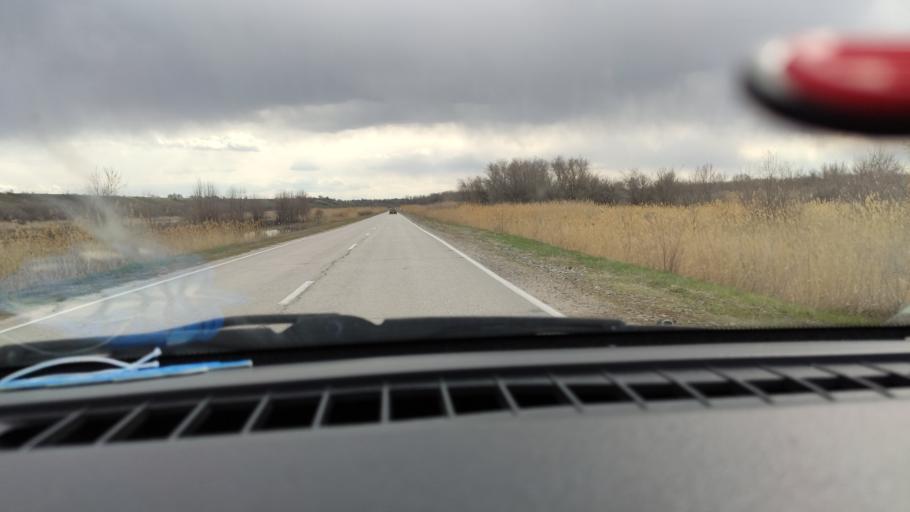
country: RU
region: Saratov
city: Privolzhskiy
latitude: 51.2612
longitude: 45.9454
